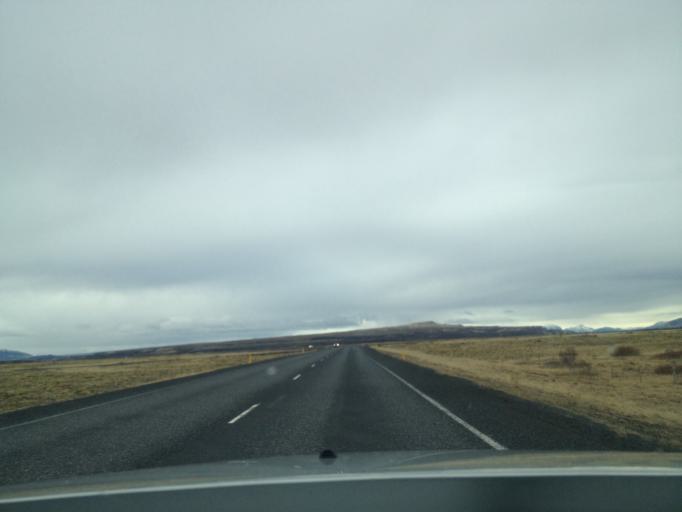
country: IS
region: South
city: Selfoss
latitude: 63.9360
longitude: -20.6696
